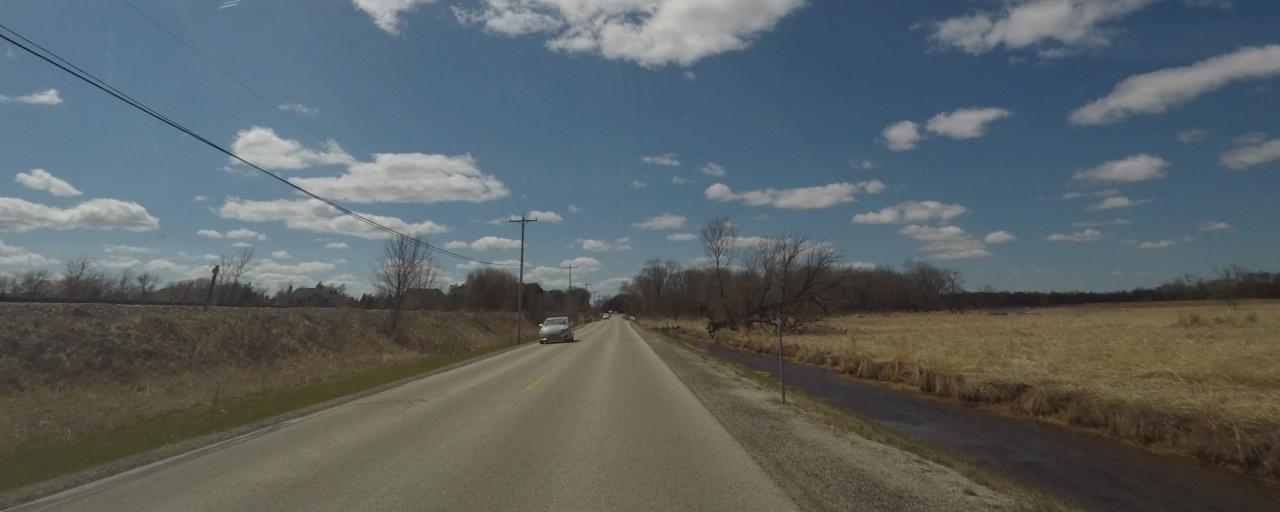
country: US
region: Wisconsin
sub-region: Waukesha County
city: Brookfield
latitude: 43.0726
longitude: -88.1610
